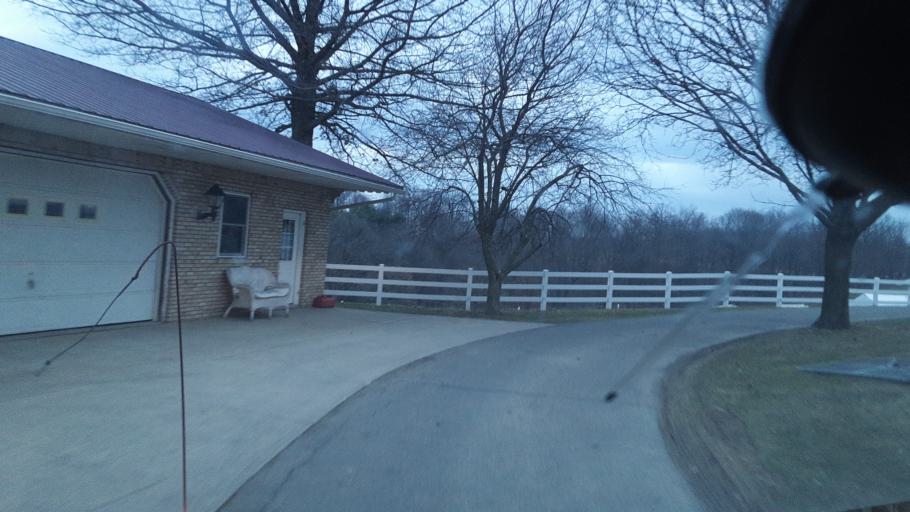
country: US
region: Ohio
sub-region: Tuscarawas County
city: Sugarcreek
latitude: 40.4990
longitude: -81.6791
